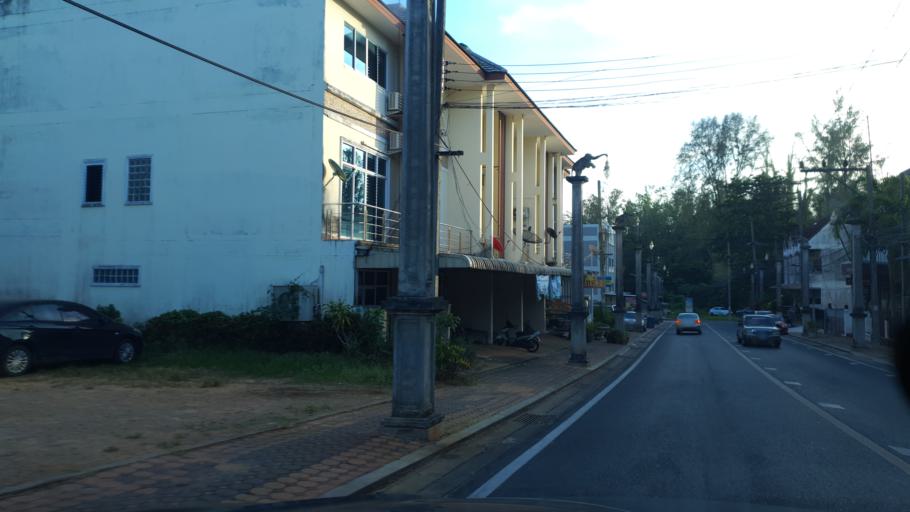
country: TH
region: Krabi
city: Krabi
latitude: 8.0544
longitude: 98.9170
